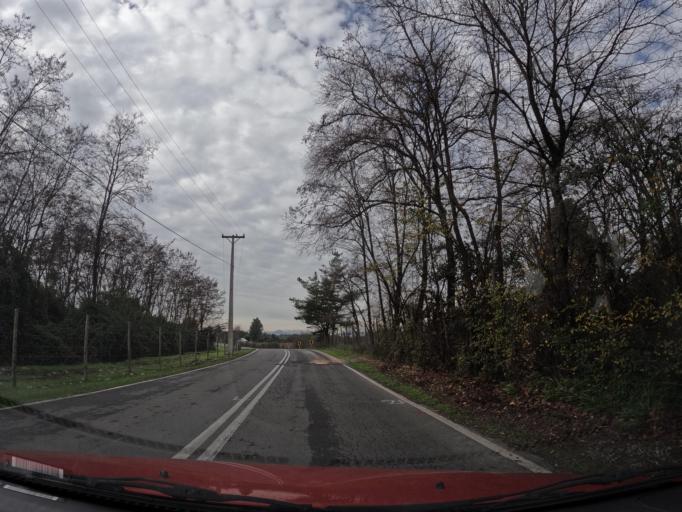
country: CL
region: Maule
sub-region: Provincia de Linares
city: Linares
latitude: -35.8660
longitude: -71.6241
